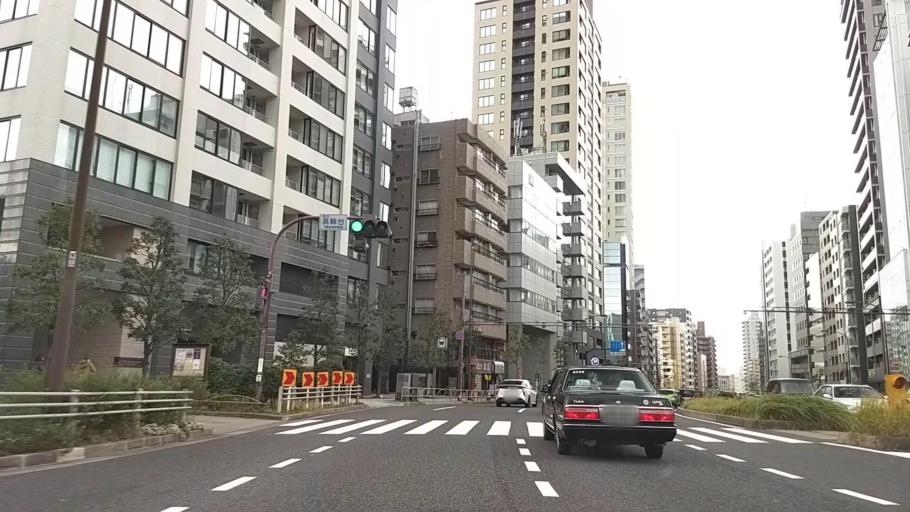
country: JP
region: Tokyo
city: Tokyo
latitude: 35.6321
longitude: 139.7308
